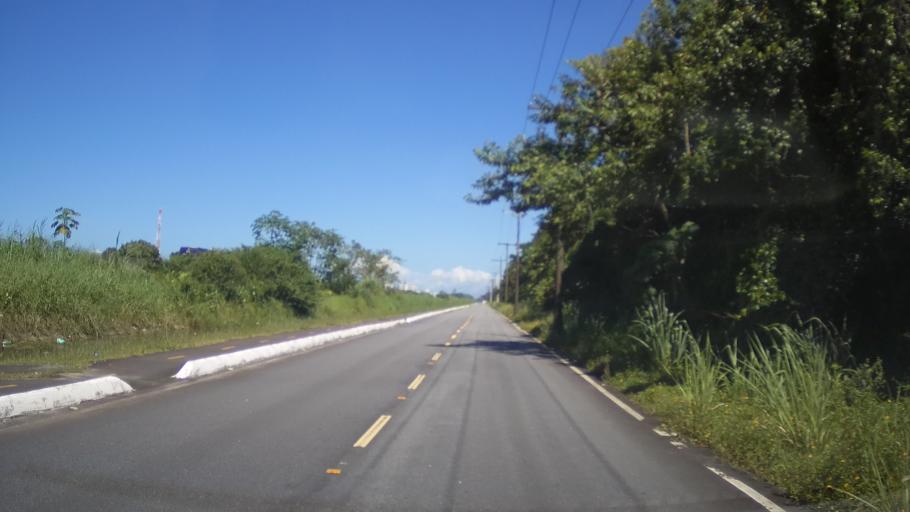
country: BR
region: Sao Paulo
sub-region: Mongagua
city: Mongagua
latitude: -24.0713
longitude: -46.5810
